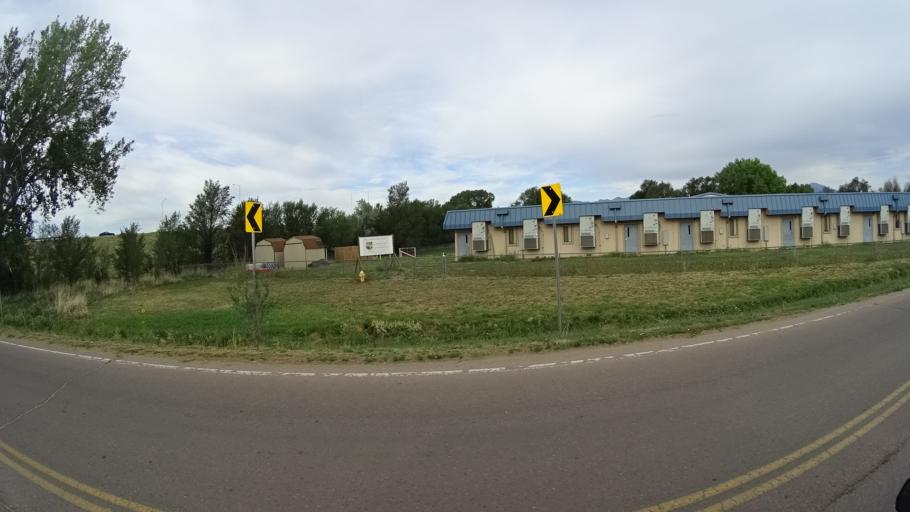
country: US
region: Colorado
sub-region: El Paso County
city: Security-Widefield
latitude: 38.7239
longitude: -104.7150
